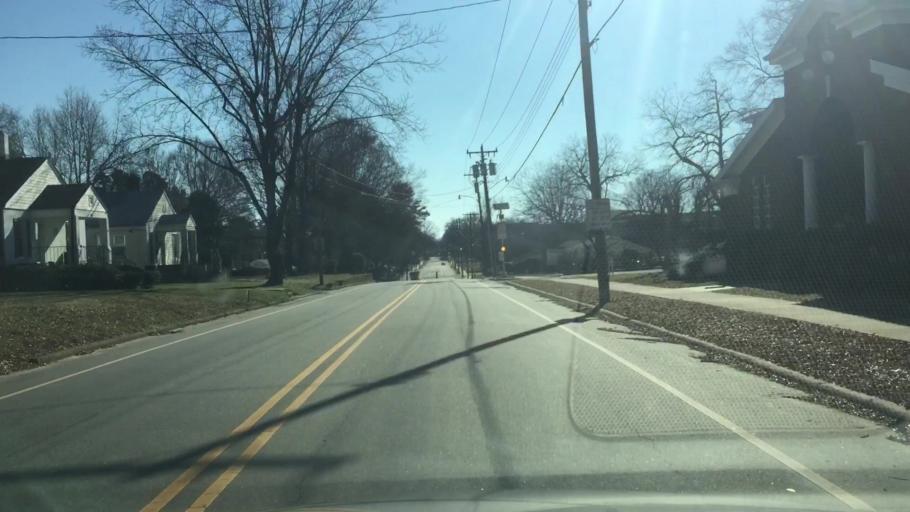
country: US
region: North Carolina
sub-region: Iredell County
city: Mooresville
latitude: 35.5806
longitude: -80.8008
